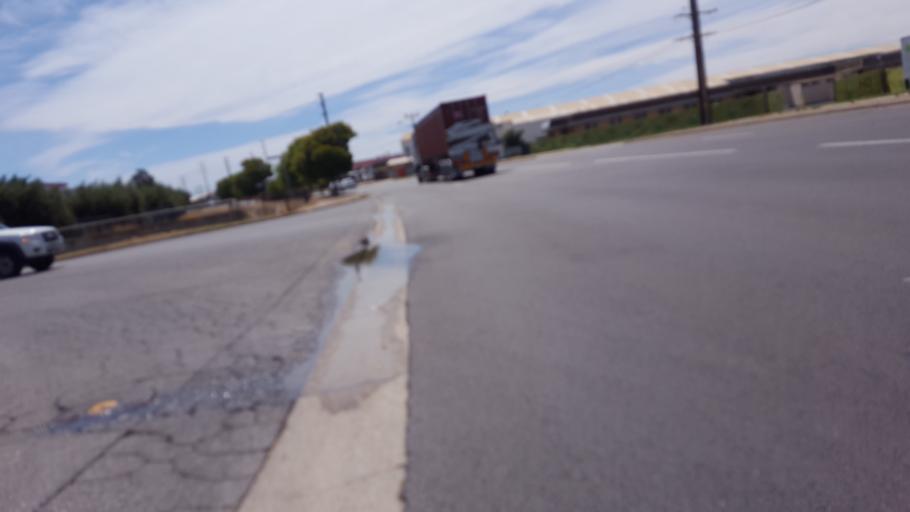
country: AU
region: South Australia
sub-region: Port Adelaide Enfield
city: Alberton
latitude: -34.8417
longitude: 138.5299
